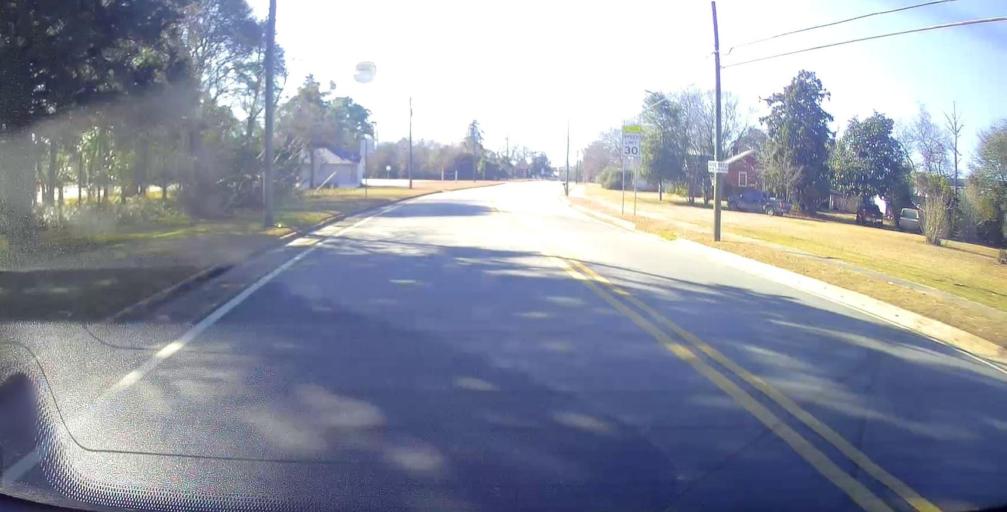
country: US
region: Georgia
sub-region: Taylor County
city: Butler
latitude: 32.5560
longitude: -84.2318
